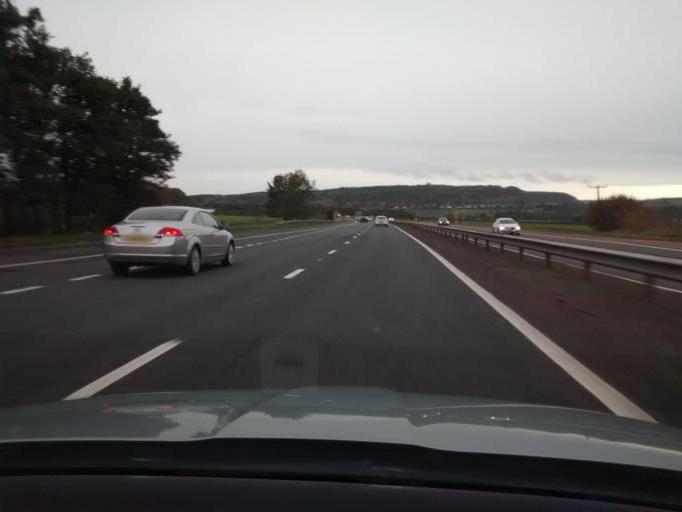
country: GB
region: Scotland
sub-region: Stirling
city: Stirling
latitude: 56.1285
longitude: -3.9708
